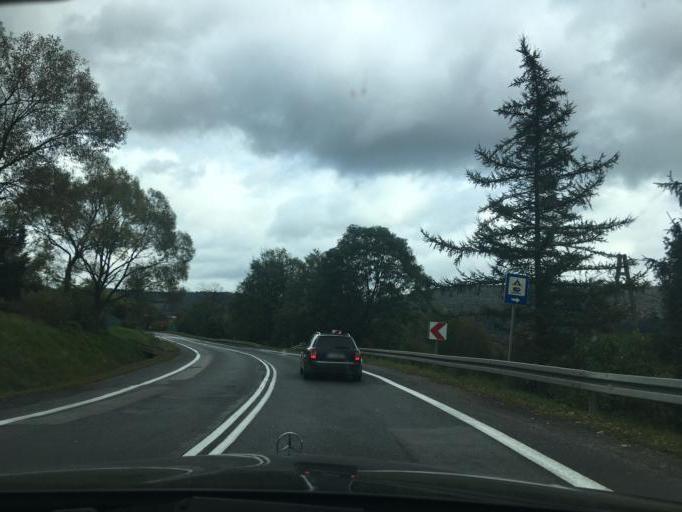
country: PL
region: Subcarpathian Voivodeship
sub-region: Powiat krosnienski
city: Dukla
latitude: 49.4717
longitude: 21.7066
